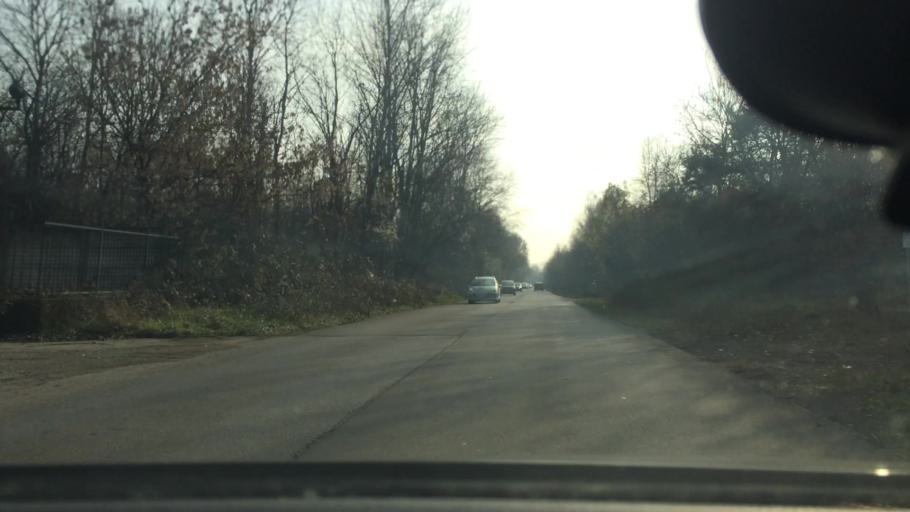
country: IT
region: Lombardy
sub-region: Provincia di Monza e Brianza
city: Villaggio del Sole
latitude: 45.6030
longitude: 9.0960
